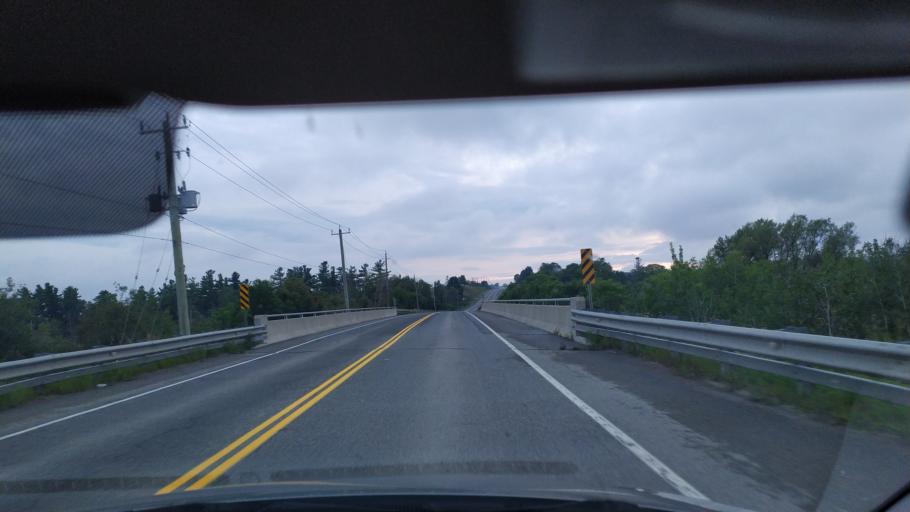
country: CA
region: Ontario
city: Cambridge
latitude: 43.3359
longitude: -80.4209
